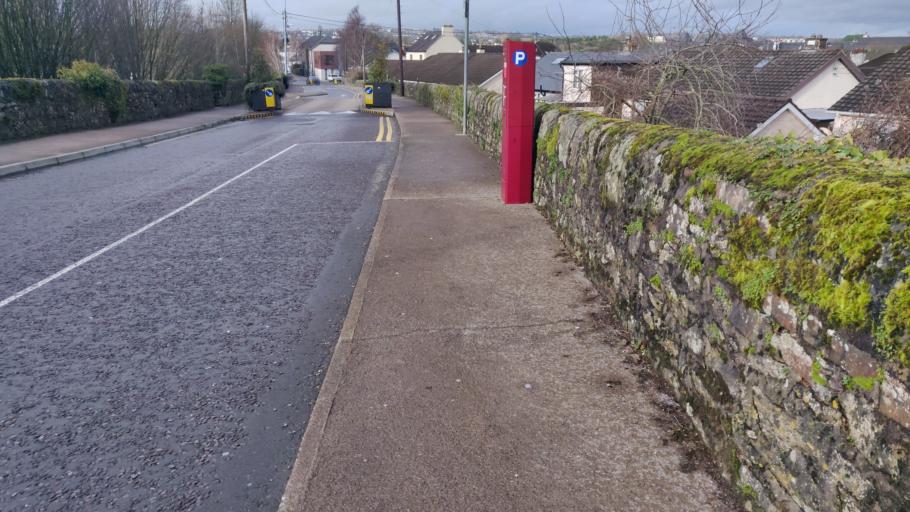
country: IE
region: Munster
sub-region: County Cork
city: Cork
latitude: 51.8747
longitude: -8.4348
